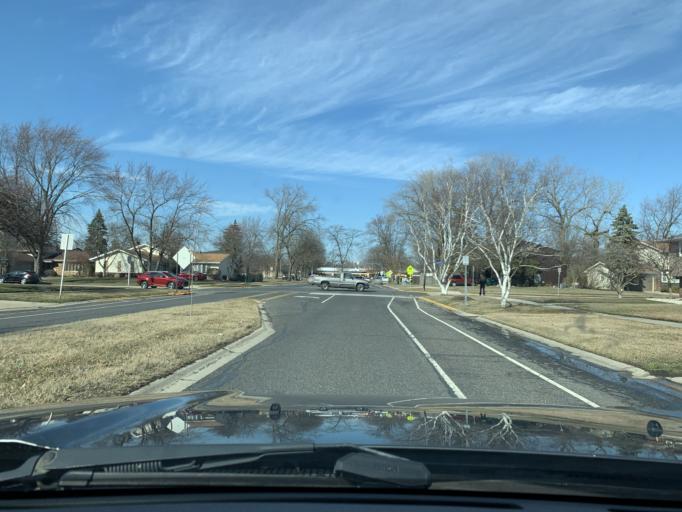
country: US
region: Indiana
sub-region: Lake County
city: Munster
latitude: 41.5406
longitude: -87.4993
